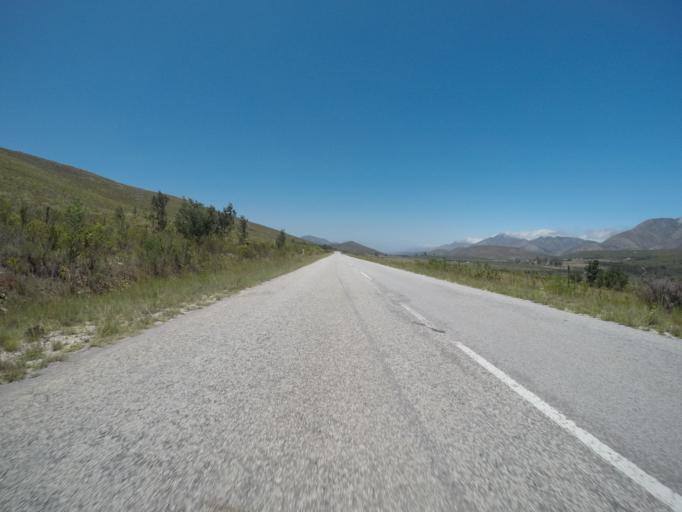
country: ZA
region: Eastern Cape
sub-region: Cacadu District Municipality
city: Kareedouw
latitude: -33.8488
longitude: 23.9656
